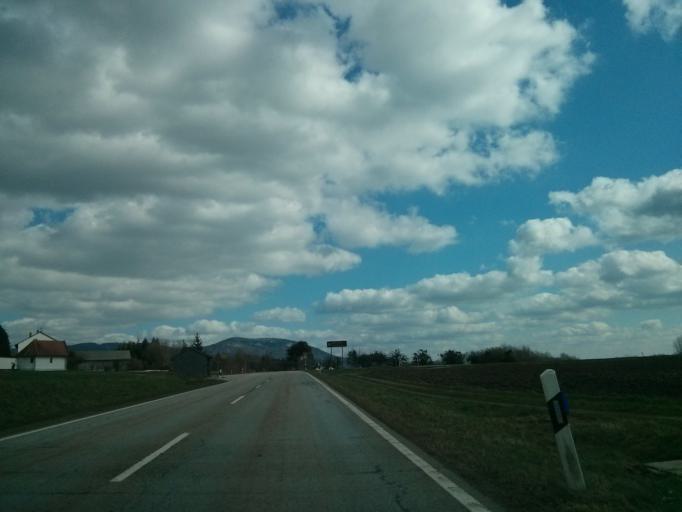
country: DE
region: Bavaria
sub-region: Lower Bavaria
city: Schaufling
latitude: 48.8467
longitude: 13.1002
